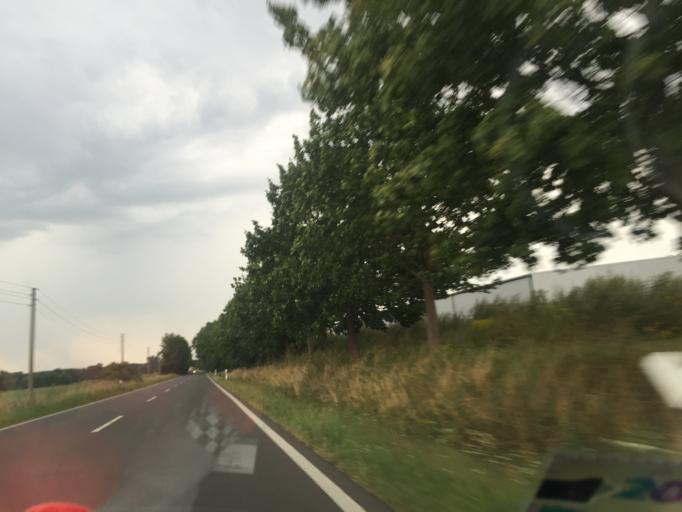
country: DE
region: Brandenburg
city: Zehdenick
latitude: 52.9898
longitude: 13.3058
